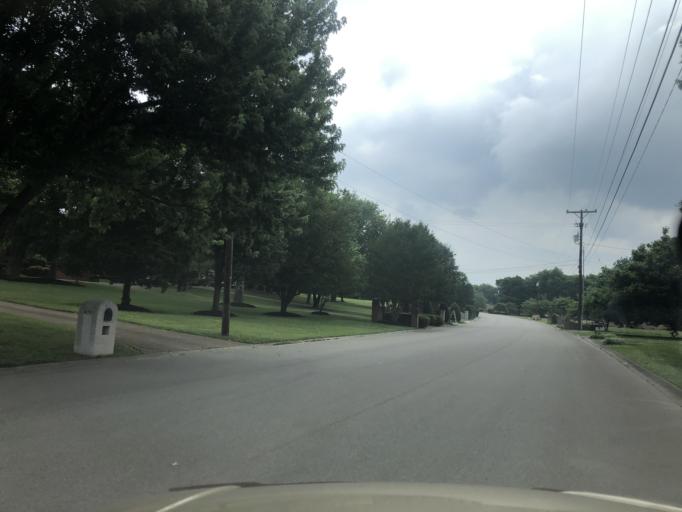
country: US
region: Tennessee
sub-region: Davidson County
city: Lakewood
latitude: 36.2336
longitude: -86.6146
